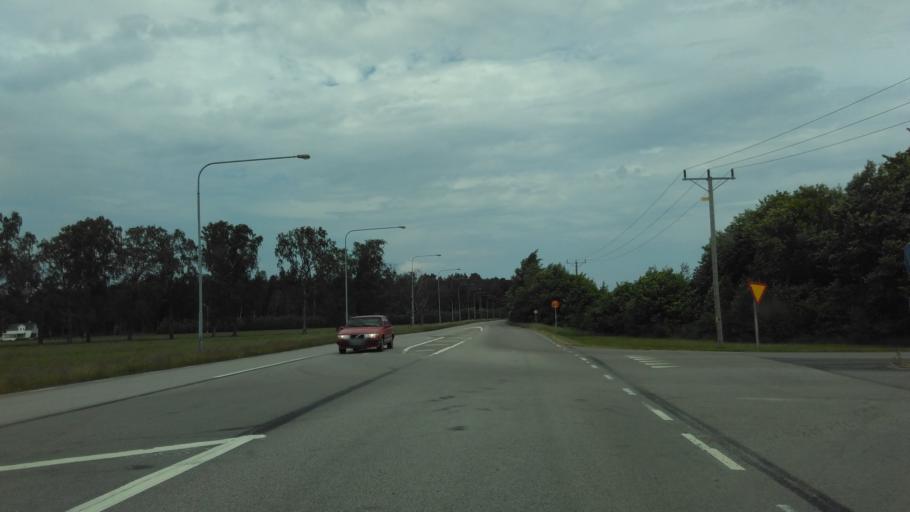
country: SE
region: Vaestra Goetaland
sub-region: Lidkopings Kommun
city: Lidkoping
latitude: 58.4810
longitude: 13.1370
